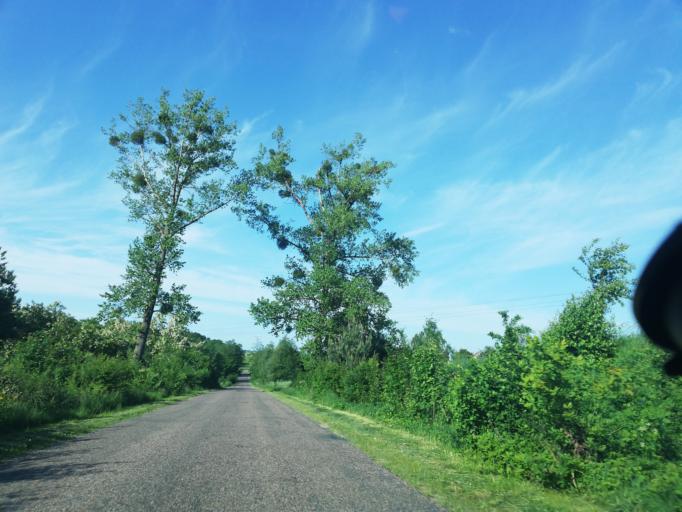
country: PL
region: Kujawsko-Pomorskie
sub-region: Powiat golubsko-dobrzynski
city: Golub-Dobrzyn
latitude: 53.0346
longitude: 19.0776
